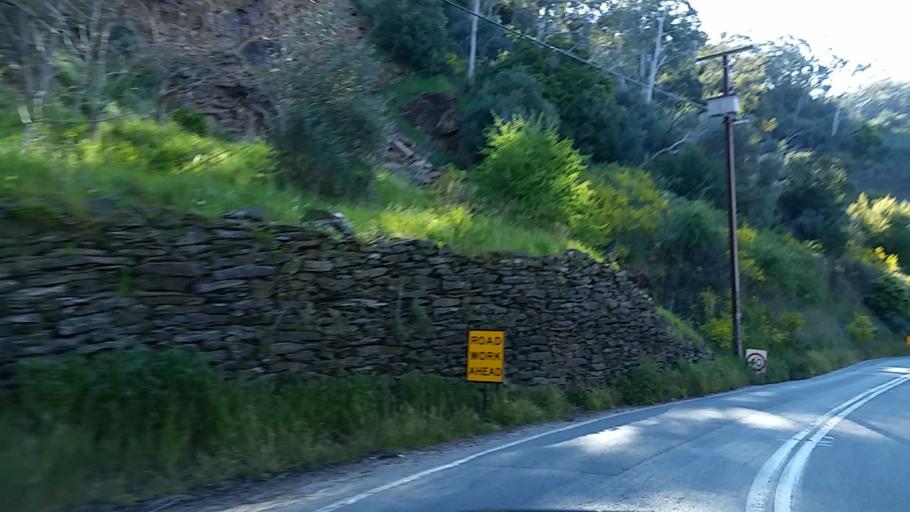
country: AU
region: South Australia
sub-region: Adelaide Hills
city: Adelaide Hills
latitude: -34.9270
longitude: 138.7193
